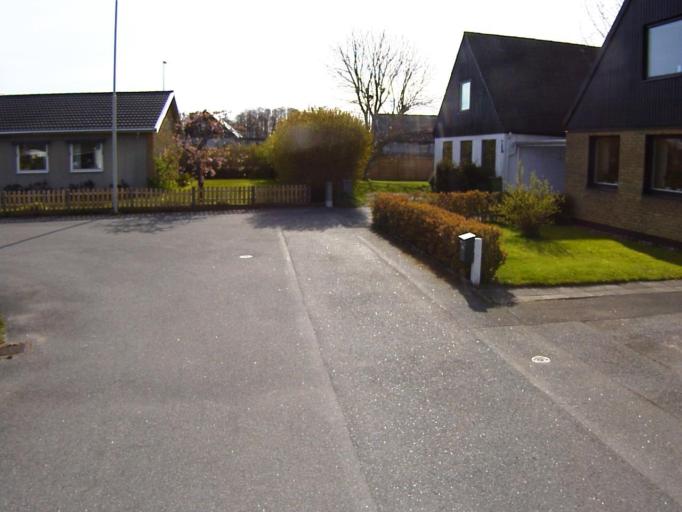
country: SE
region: Skane
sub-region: Kristianstads Kommun
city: Kristianstad
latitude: 56.0088
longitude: 14.1511
